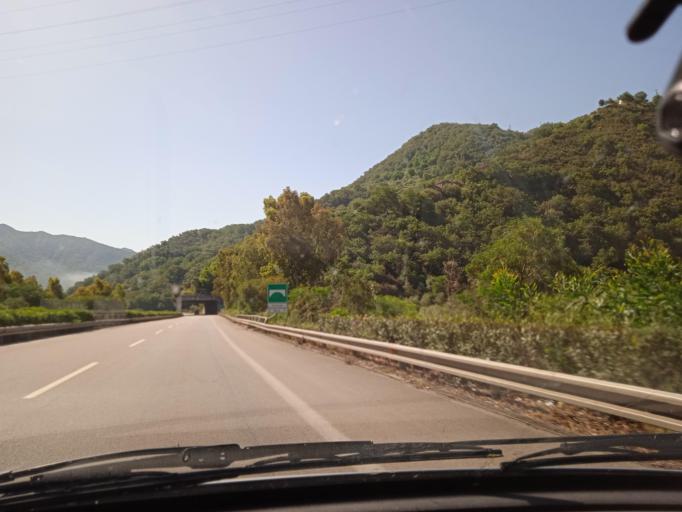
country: IT
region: Sicily
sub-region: Messina
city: Piraino
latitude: 38.1487
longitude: 14.8543
